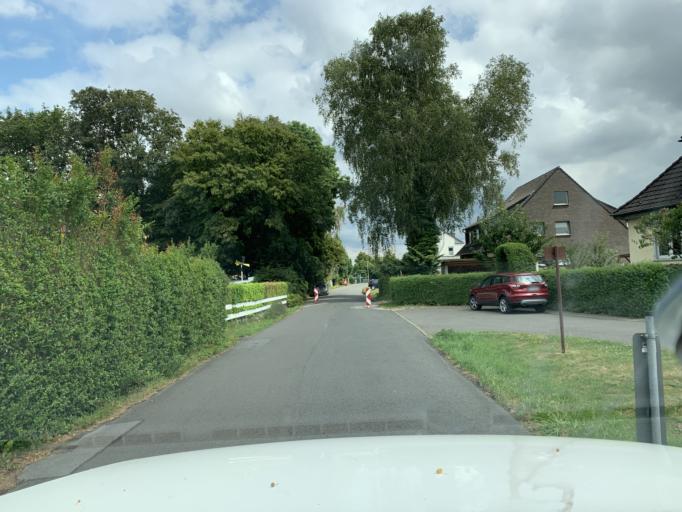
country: DE
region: North Rhine-Westphalia
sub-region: Regierungsbezirk Dusseldorf
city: Muelheim (Ruhr)
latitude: 51.4454
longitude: 6.9350
